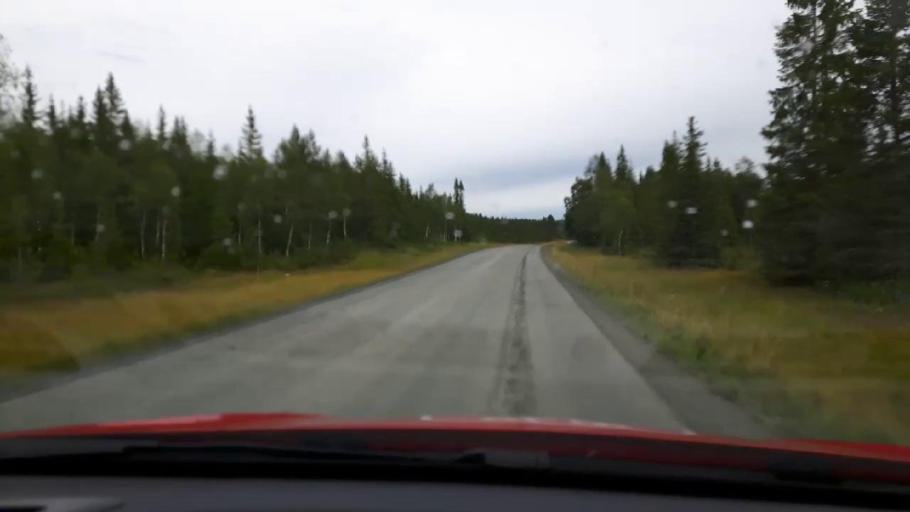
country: SE
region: Jaemtland
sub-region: Are Kommun
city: Are
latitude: 63.4389
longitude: 13.2577
